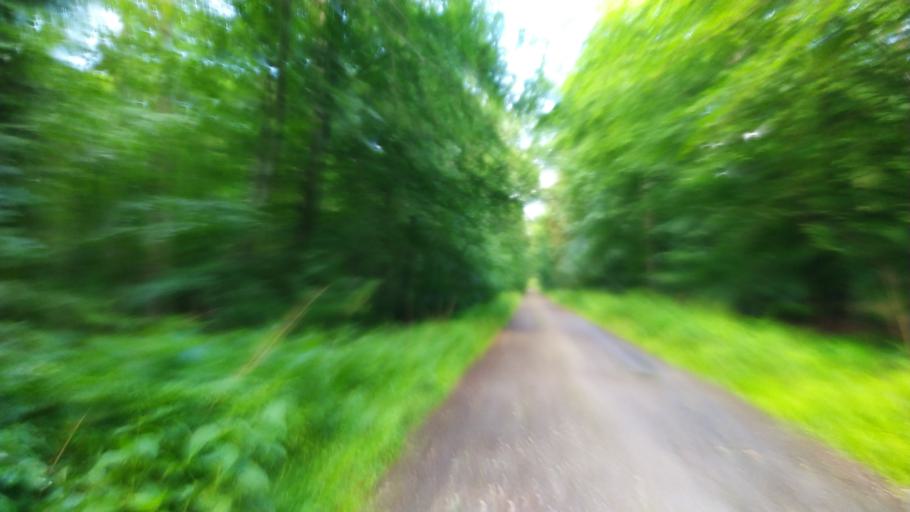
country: DE
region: Lower Saxony
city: Deinstedt
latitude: 53.4391
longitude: 9.2120
